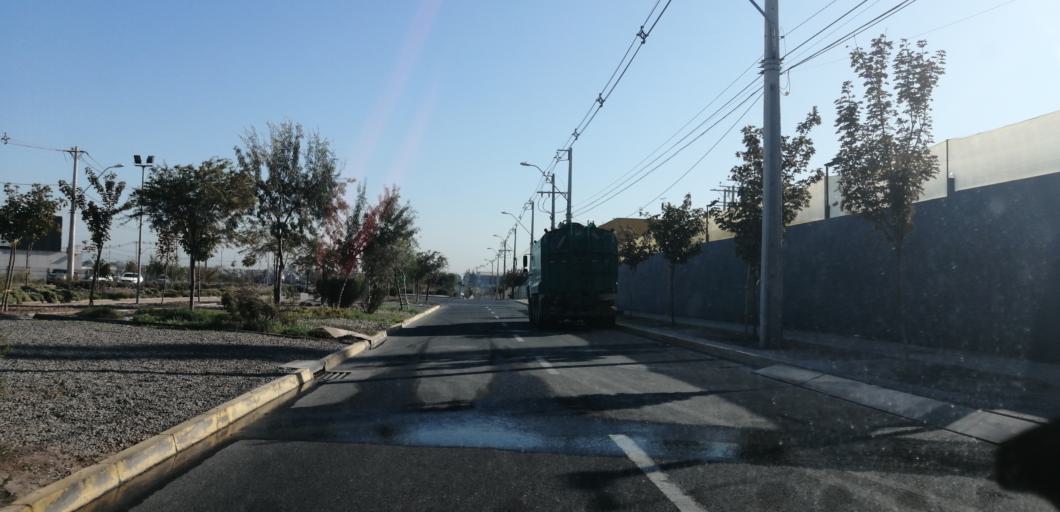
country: CL
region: Santiago Metropolitan
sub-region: Provincia de Santiago
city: Lo Prado
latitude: -33.4416
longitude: -70.7753
